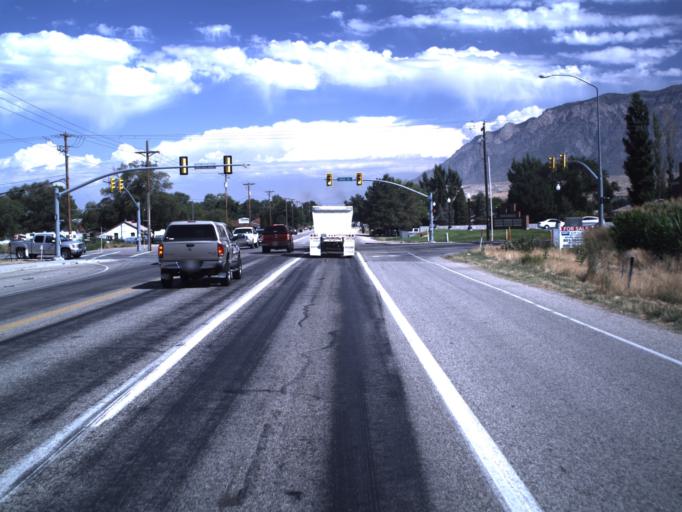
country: US
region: Utah
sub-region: Weber County
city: Farr West
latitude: 41.2889
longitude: -112.0278
